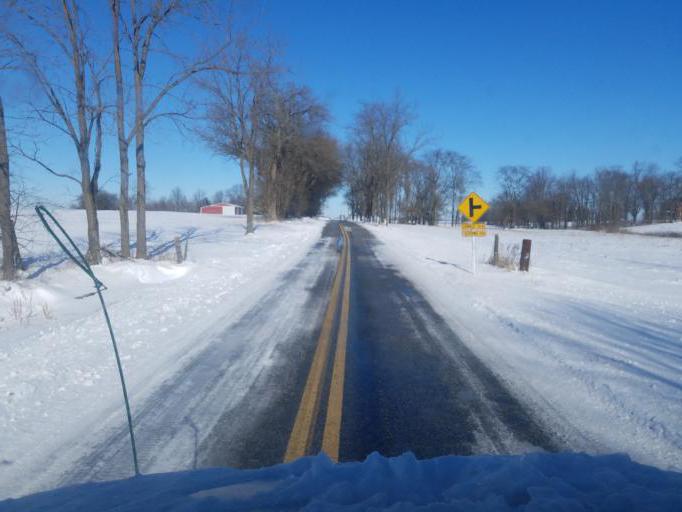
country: US
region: Ohio
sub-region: Delaware County
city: Delaware
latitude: 40.3016
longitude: -82.9888
